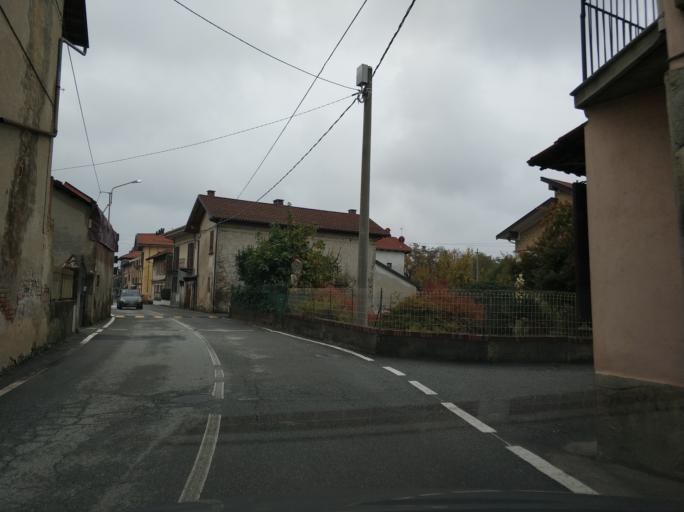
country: IT
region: Piedmont
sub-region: Provincia di Torino
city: Villanova Canavese
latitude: 45.2439
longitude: 7.5478
